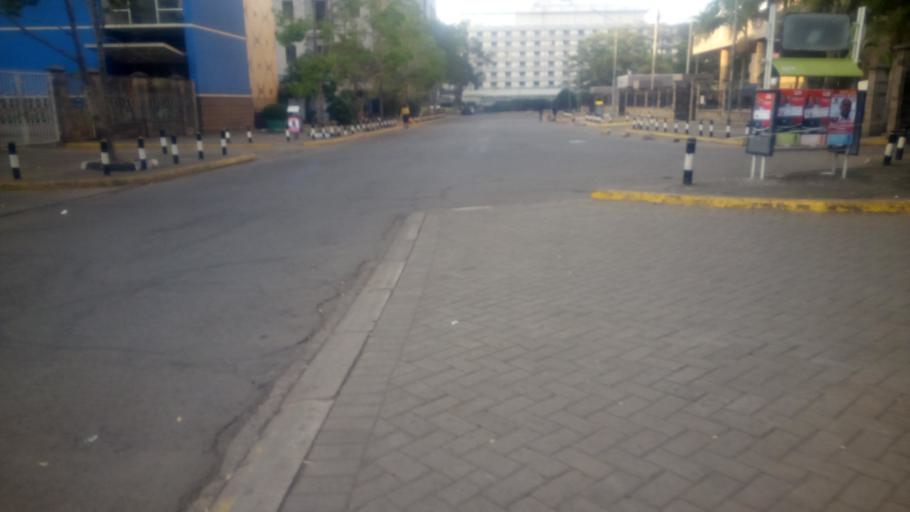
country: KE
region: Nairobi Area
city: Nairobi
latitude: -1.2864
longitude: 36.8184
